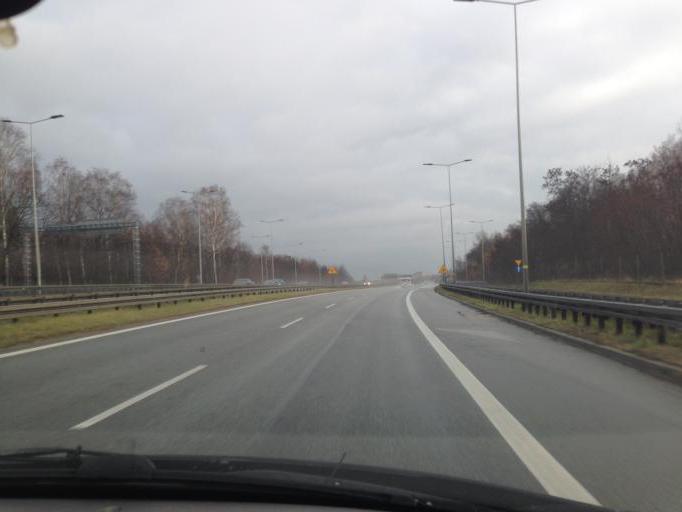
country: PL
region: Silesian Voivodeship
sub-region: Katowice
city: Katowice
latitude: 50.2380
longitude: 19.0594
